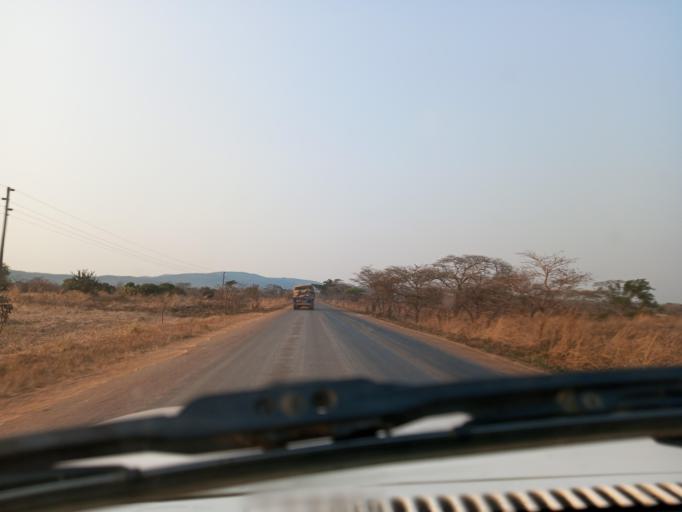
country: ZM
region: Northern
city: Mpika
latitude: -11.9279
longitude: 31.4180
